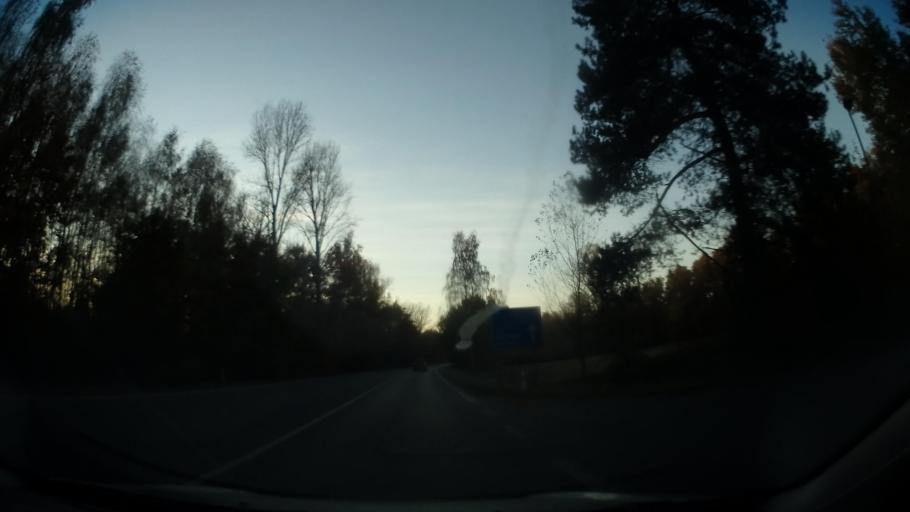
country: CZ
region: Pardubicky
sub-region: Okres Pardubice
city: Lazne Bohdanec
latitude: 50.0861
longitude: 15.6653
